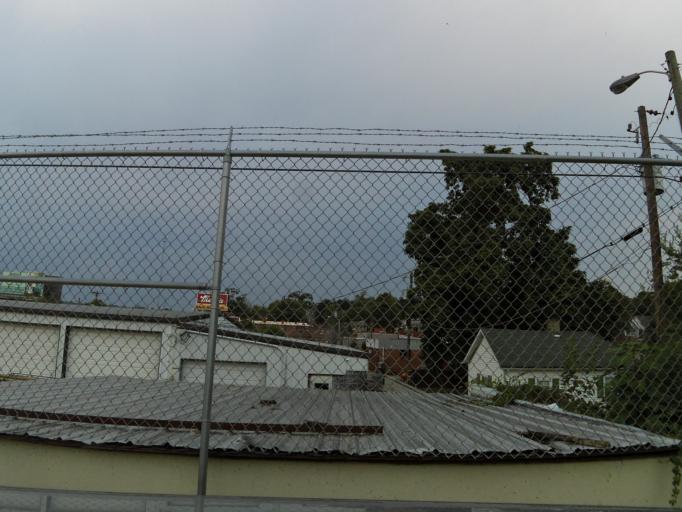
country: US
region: Tennessee
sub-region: Knox County
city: Knoxville
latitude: 35.9814
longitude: -83.9283
